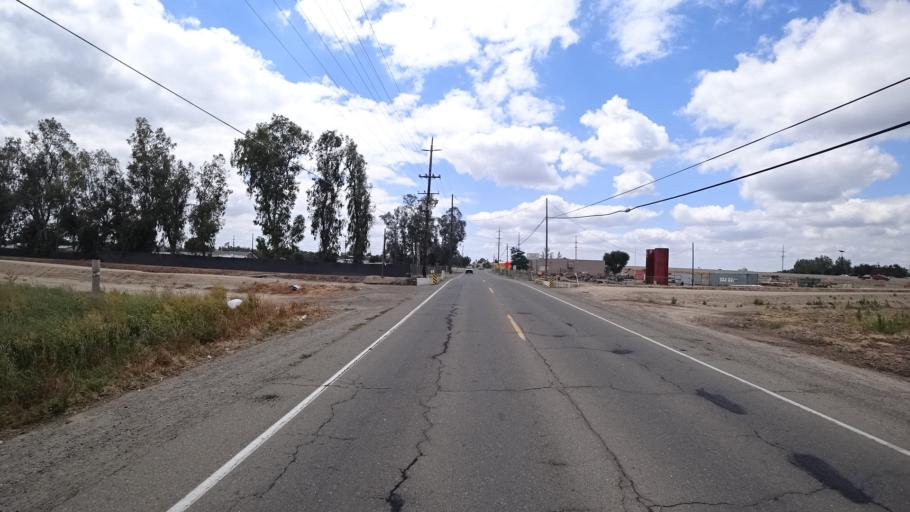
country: US
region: California
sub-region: Kings County
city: Armona
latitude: 36.3135
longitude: -119.6886
